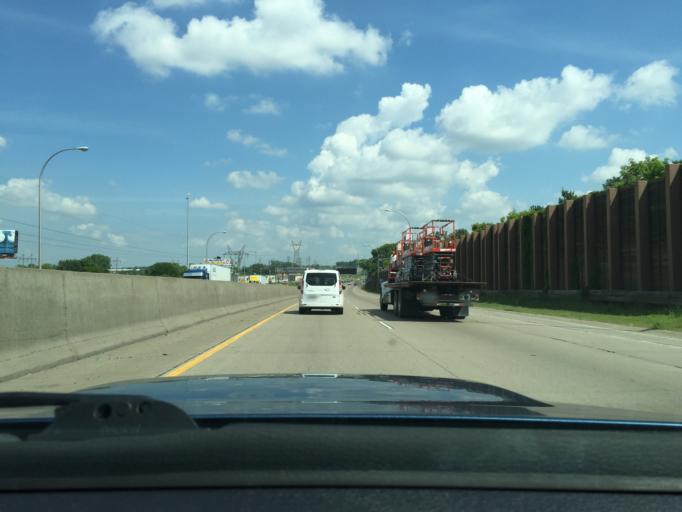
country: US
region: Minnesota
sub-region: Ramsey County
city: Lauderdale
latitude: 44.9784
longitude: -93.2029
